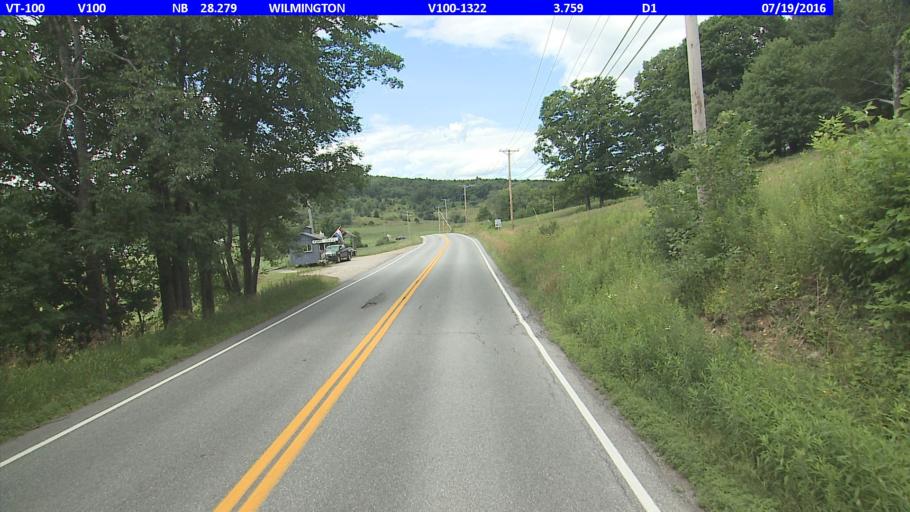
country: US
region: Vermont
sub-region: Windham County
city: Dover
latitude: 42.8836
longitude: -72.8650
